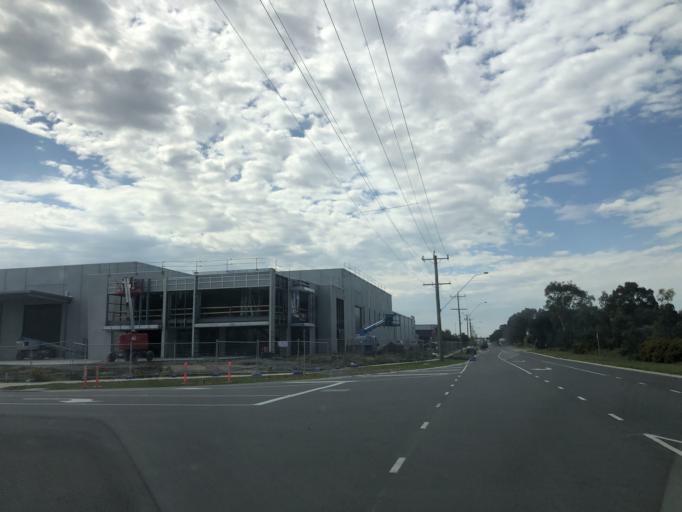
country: AU
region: Victoria
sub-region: Casey
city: Hampton Park
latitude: -38.0415
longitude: 145.2275
